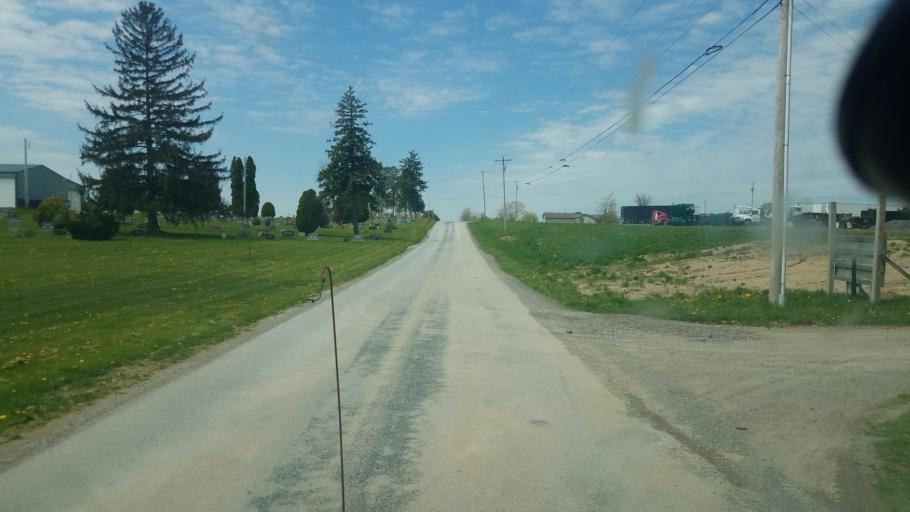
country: US
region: Ohio
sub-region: Hardin County
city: Ada
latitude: 40.7114
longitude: -83.8212
